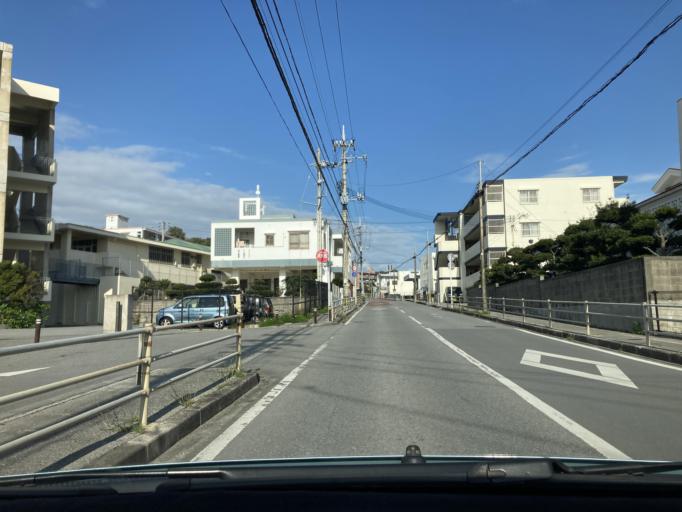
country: JP
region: Okinawa
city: Tomigusuku
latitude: 26.1656
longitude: 127.6735
